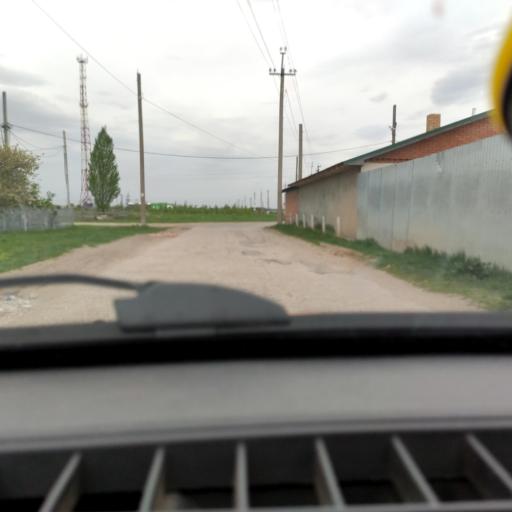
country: RU
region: Samara
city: Povolzhskiy
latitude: 53.6450
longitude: 49.6833
